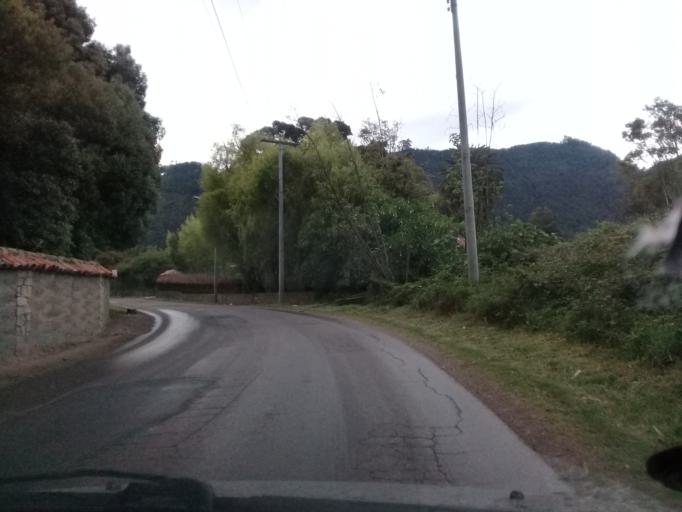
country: CO
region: Cundinamarca
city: Cajica
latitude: 4.9270
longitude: -74.0483
